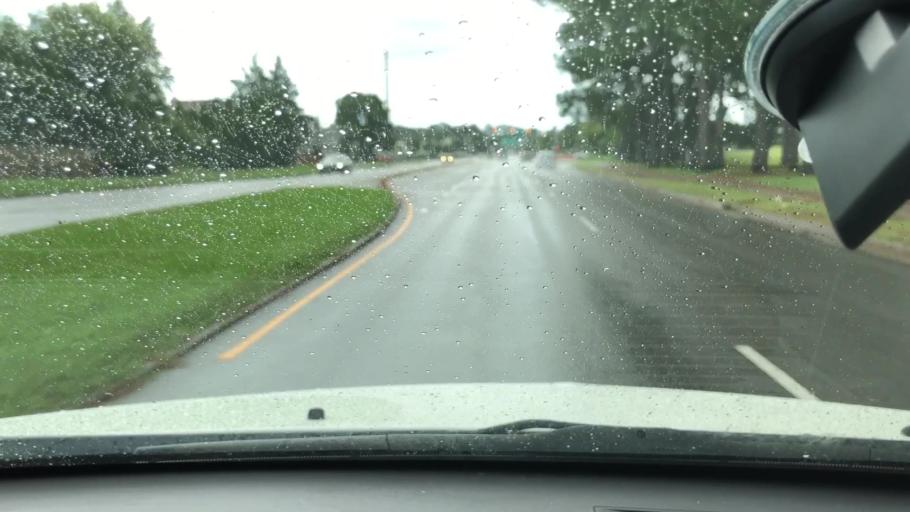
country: US
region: Virginia
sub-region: City of Chesapeake
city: Chesapeake
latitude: 36.8270
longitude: -76.1440
